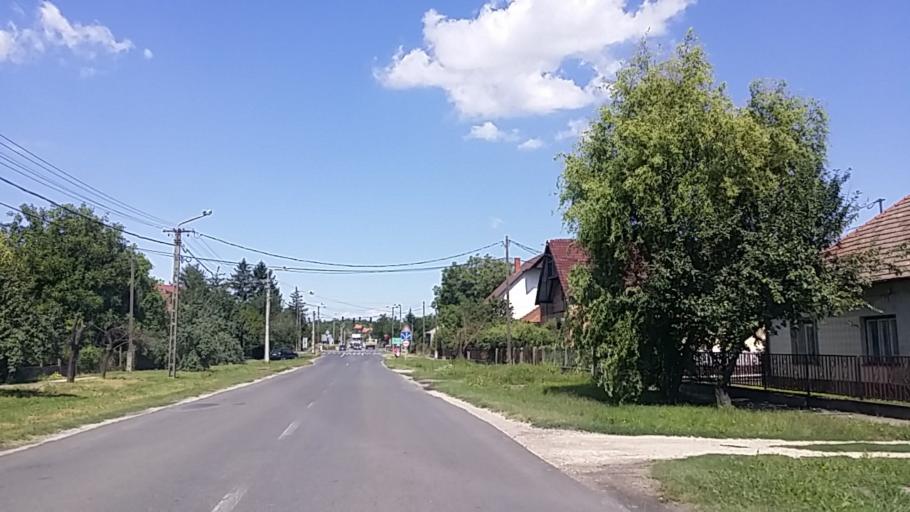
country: HU
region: Tolna
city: Simontornya
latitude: 46.7558
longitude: 18.5442
